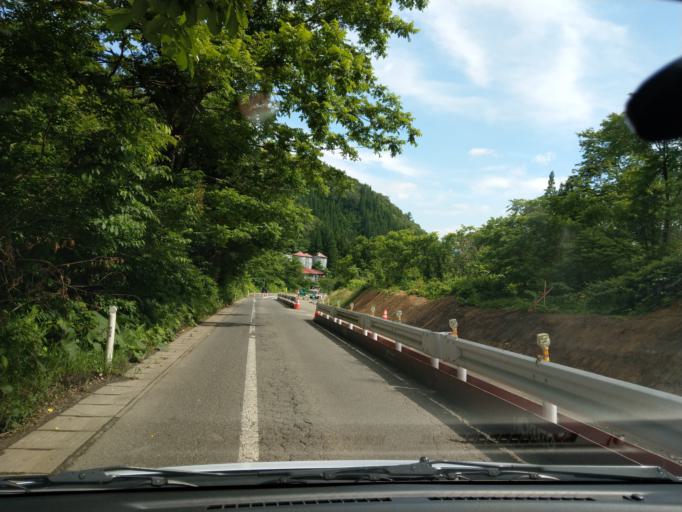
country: JP
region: Akita
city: Kakunodatemachi
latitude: 39.7231
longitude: 140.5823
